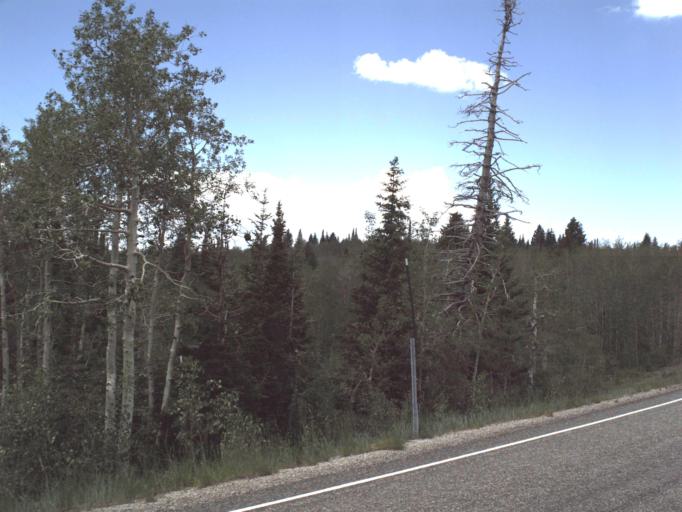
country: US
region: Utah
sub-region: Weber County
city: Wolf Creek
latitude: 41.4267
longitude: -111.5109
